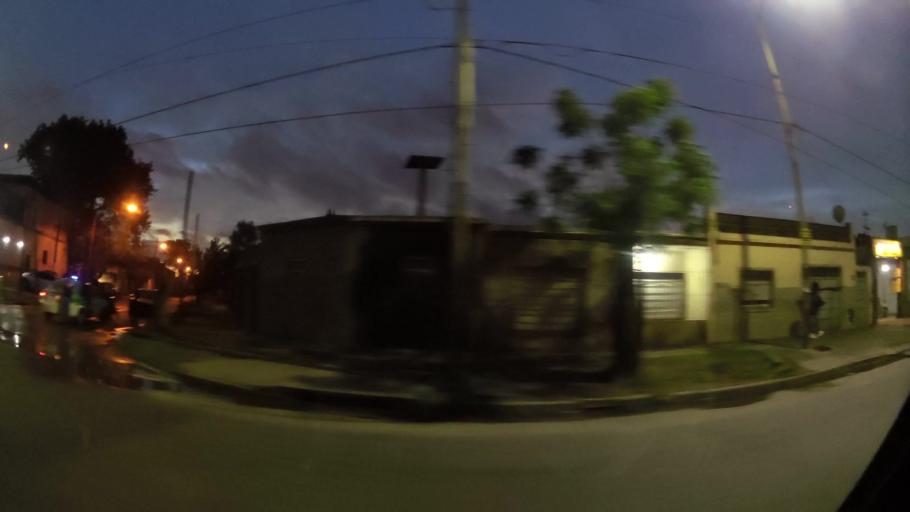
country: AR
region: Buenos Aires
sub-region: Partido de Lanus
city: Lanus
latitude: -34.7339
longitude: -58.3498
